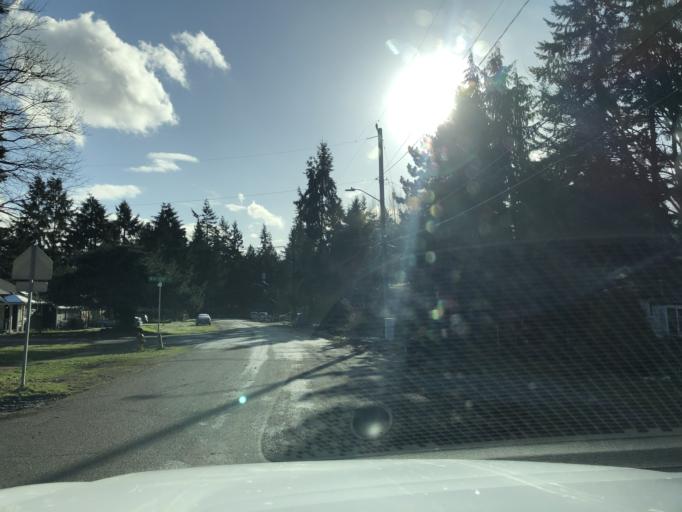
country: US
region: Washington
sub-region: King County
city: Lake Forest Park
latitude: 47.7224
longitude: -122.3047
